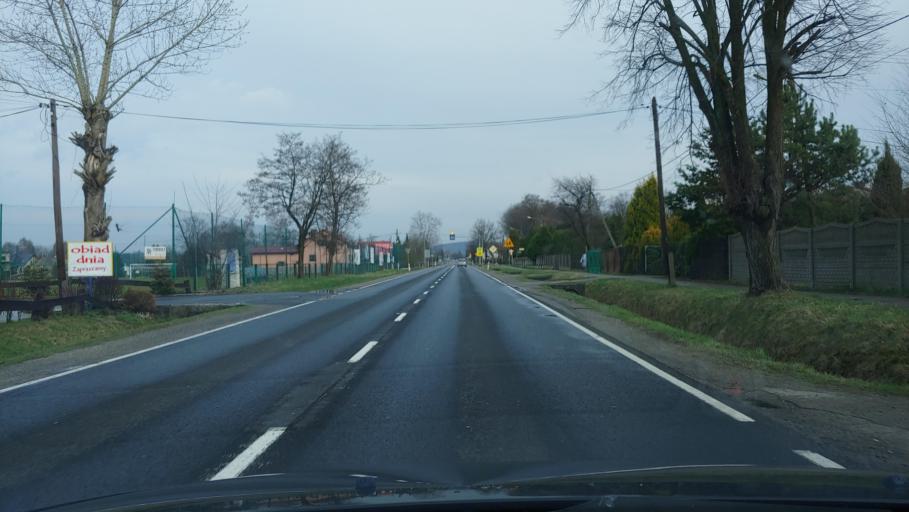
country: PL
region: Lesser Poland Voivodeship
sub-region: Powiat krakowski
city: Wola Filipowska
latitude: 50.1336
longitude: 19.5822
